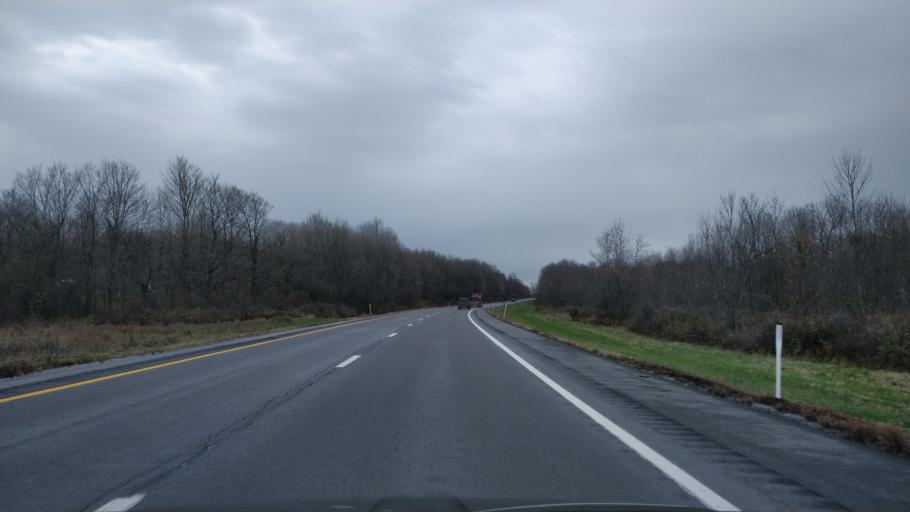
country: US
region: New York
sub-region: Jefferson County
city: Calcium
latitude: 44.1199
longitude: -75.8868
